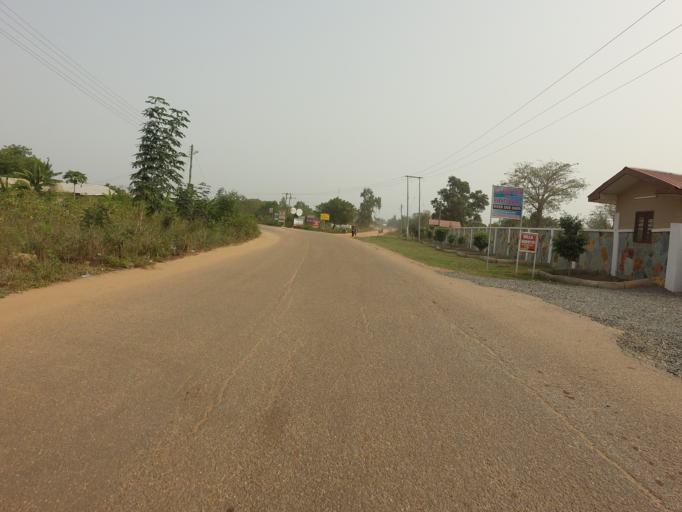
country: GH
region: Volta
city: Anloga
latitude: 5.9943
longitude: 0.5921
